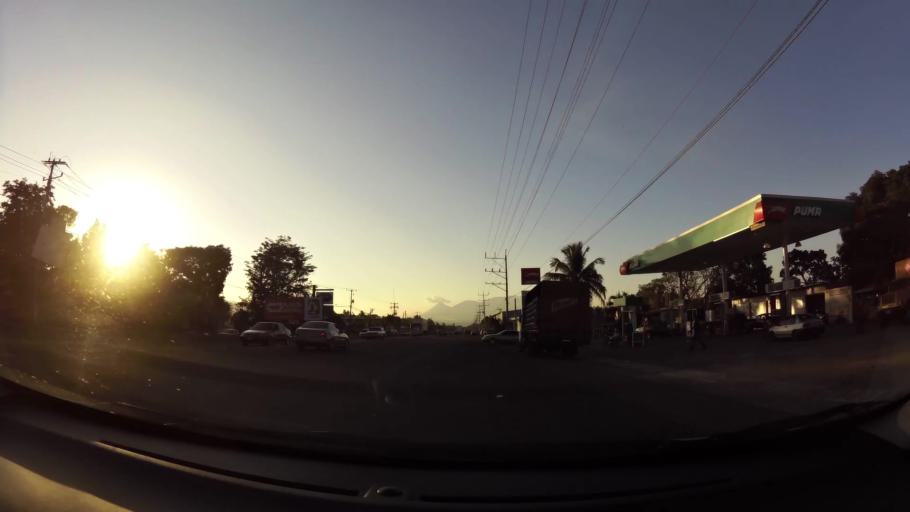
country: SV
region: Sonsonate
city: Armenia
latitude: 13.7349
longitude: -89.3917
